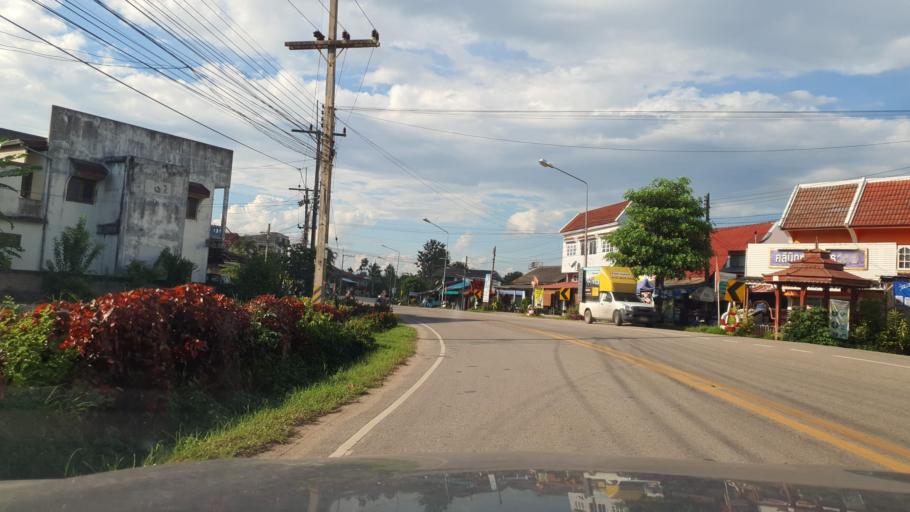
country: TH
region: Phayao
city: Phayao
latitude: 19.1474
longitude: 99.8335
